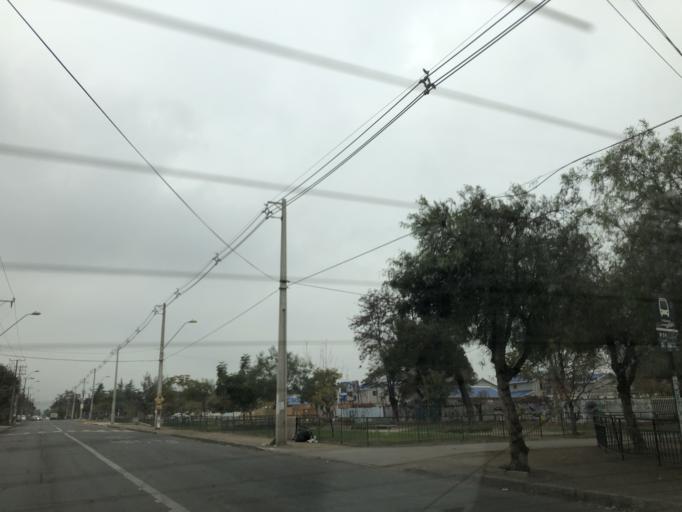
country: CL
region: Santiago Metropolitan
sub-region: Provincia de Santiago
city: La Pintana
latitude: -33.5851
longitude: -70.6083
